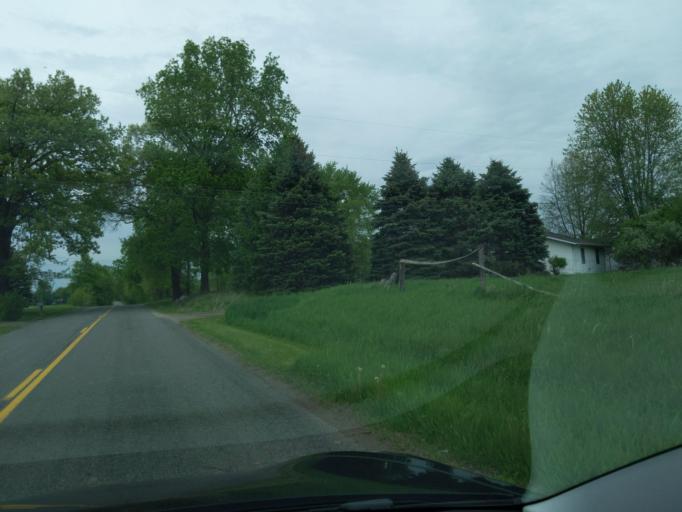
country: US
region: Michigan
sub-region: Ingham County
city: Stockbridge
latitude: 42.4312
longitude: -84.2142
